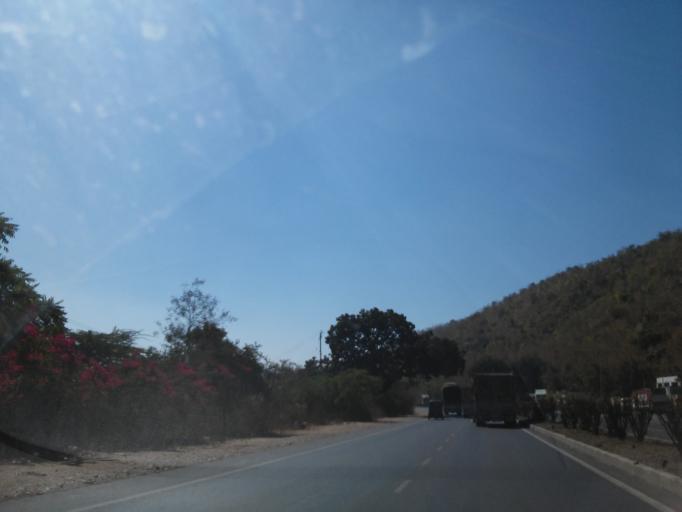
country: IN
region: Gujarat
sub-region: Sabar Kantha
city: Meghraj
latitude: 23.6975
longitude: 73.3884
